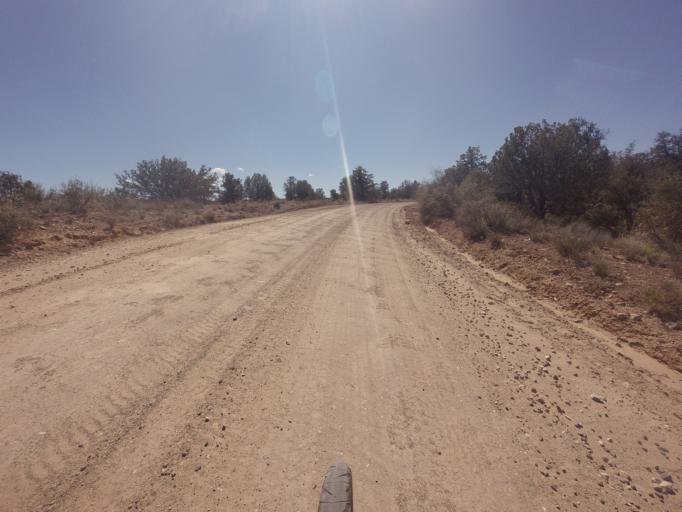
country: US
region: Arizona
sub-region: Yavapai County
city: Lake Montezuma
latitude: 34.6000
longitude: -111.7237
